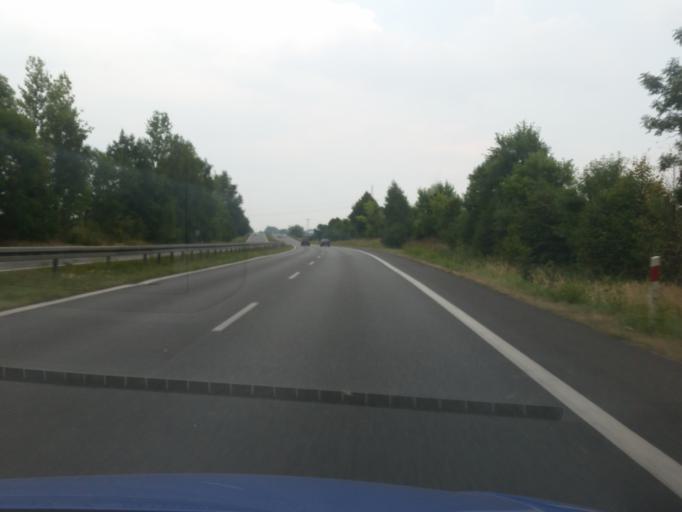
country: PL
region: Silesian Voivodeship
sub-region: Powiat bedzinski
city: Psary
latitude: 50.3596
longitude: 19.1265
